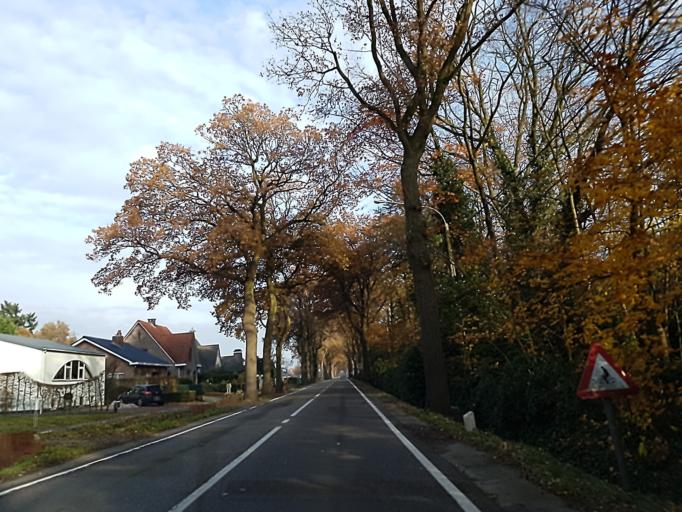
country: BE
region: Flanders
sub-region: Provincie Antwerpen
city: Essen
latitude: 51.4413
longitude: 4.4643
